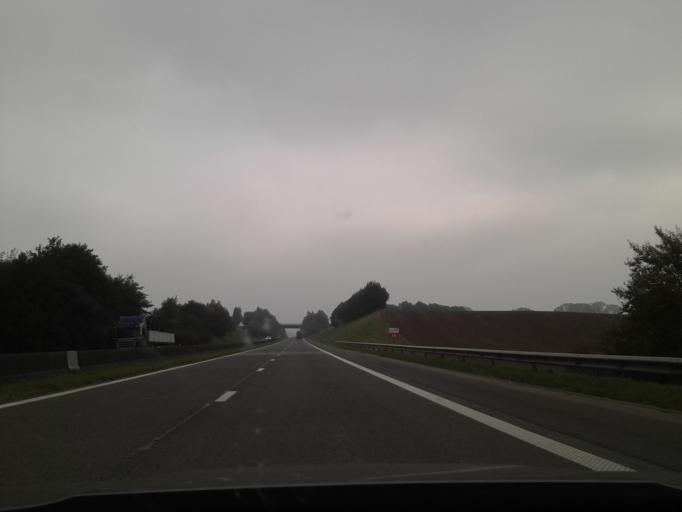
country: BE
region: Wallonia
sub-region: Province du Hainaut
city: Ath
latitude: 50.6558
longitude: 3.7223
